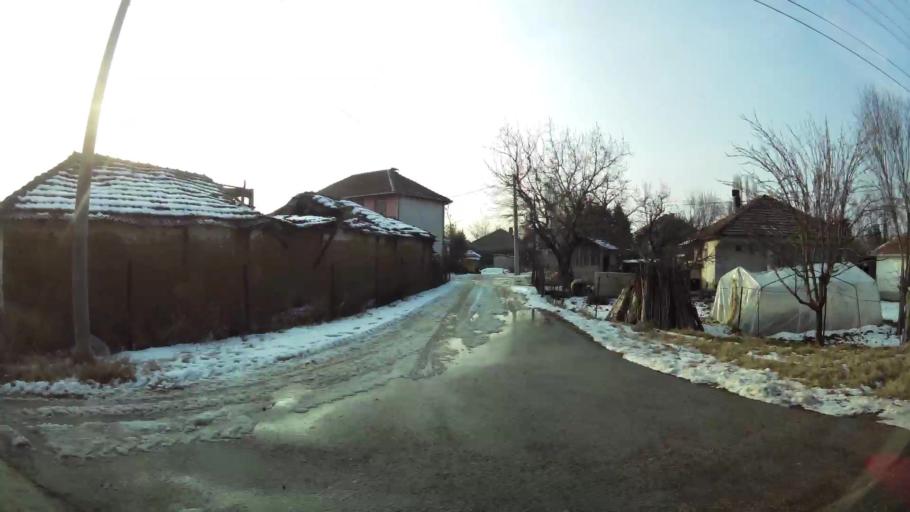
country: MK
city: Miladinovci
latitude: 41.9784
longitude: 21.6497
